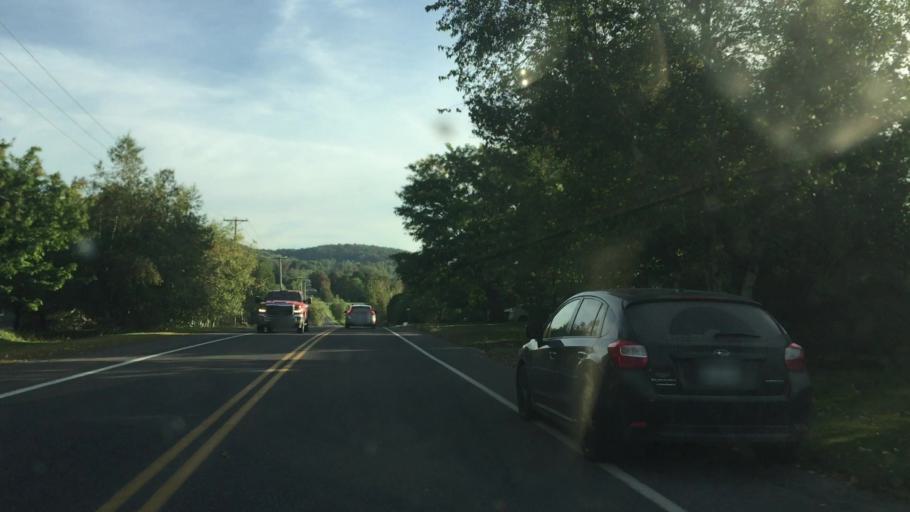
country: CA
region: Quebec
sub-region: Monteregie
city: Bromont
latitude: 45.3083
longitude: -72.6579
